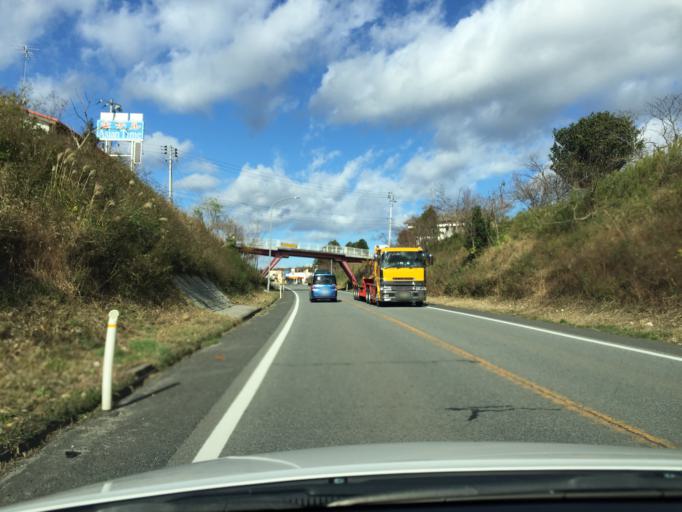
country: JP
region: Fukushima
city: Namie
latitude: 37.5009
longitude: 140.9998
